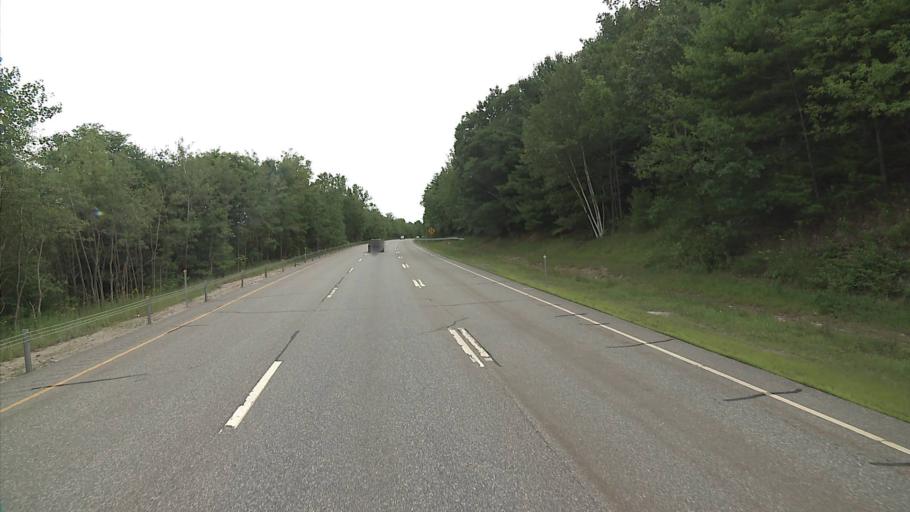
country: US
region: Connecticut
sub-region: Litchfield County
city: Torrington
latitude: 41.8479
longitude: -73.0938
